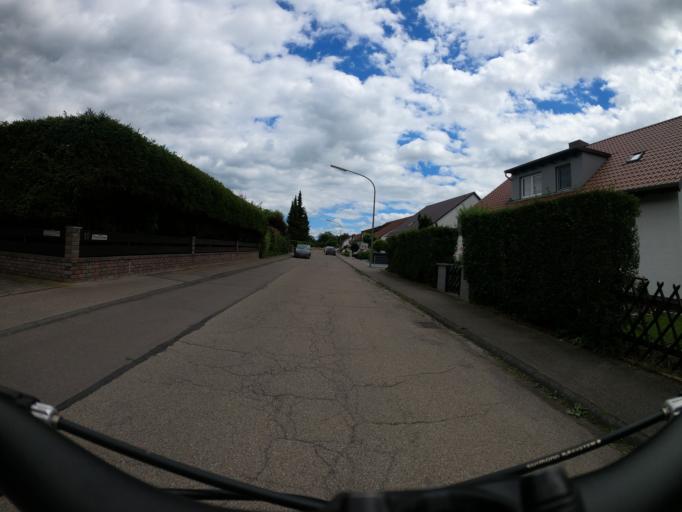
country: DE
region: Bavaria
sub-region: Swabia
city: Nersingen
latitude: 48.4328
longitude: 10.1151
